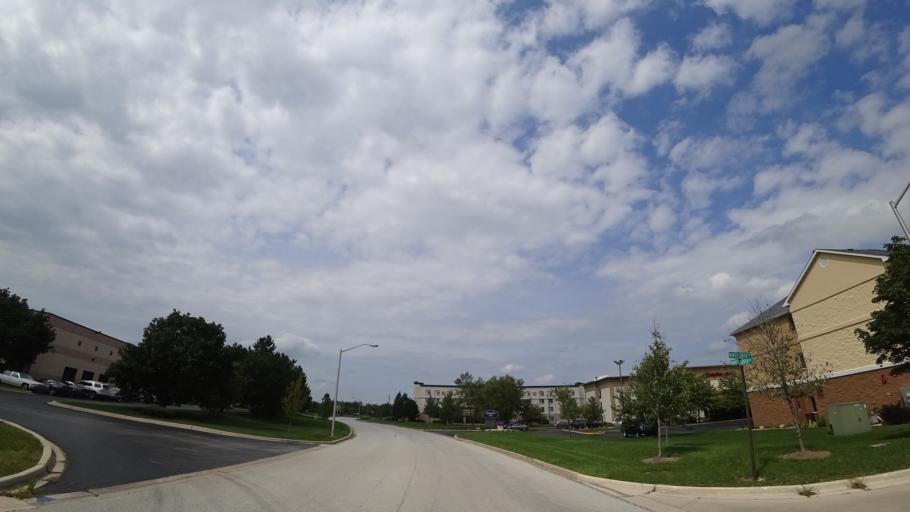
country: US
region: Illinois
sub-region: Cook County
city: Tinley Park
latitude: 41.5548
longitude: -87.7954
